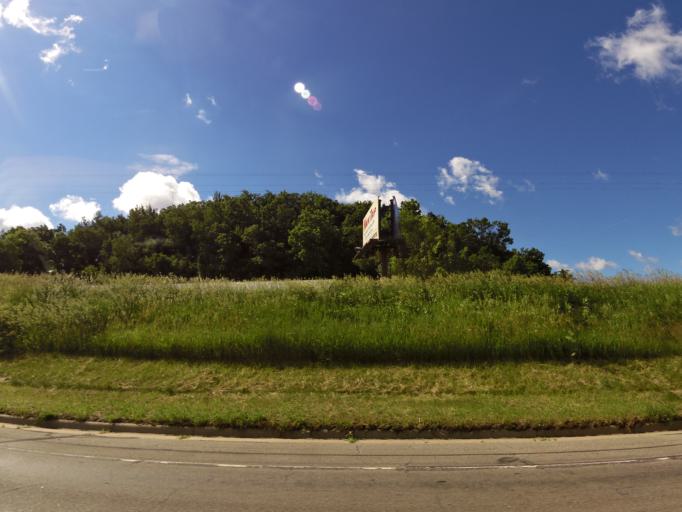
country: US
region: Minnesota
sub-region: Olmsted County
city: Rochester
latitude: 44.0099
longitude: -92.4374
